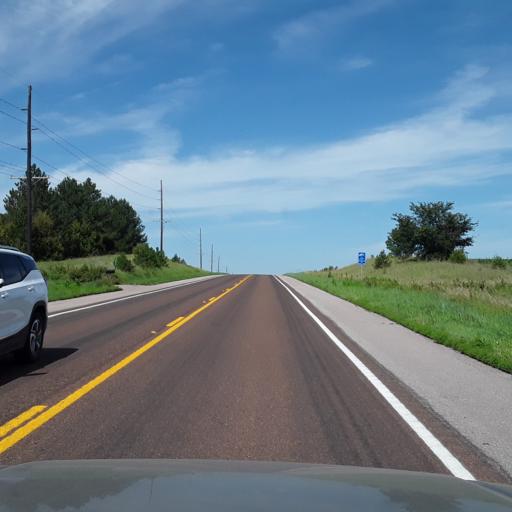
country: US
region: Nebraska
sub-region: Seward County
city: Milford
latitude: 40.8865
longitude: -96.8973
